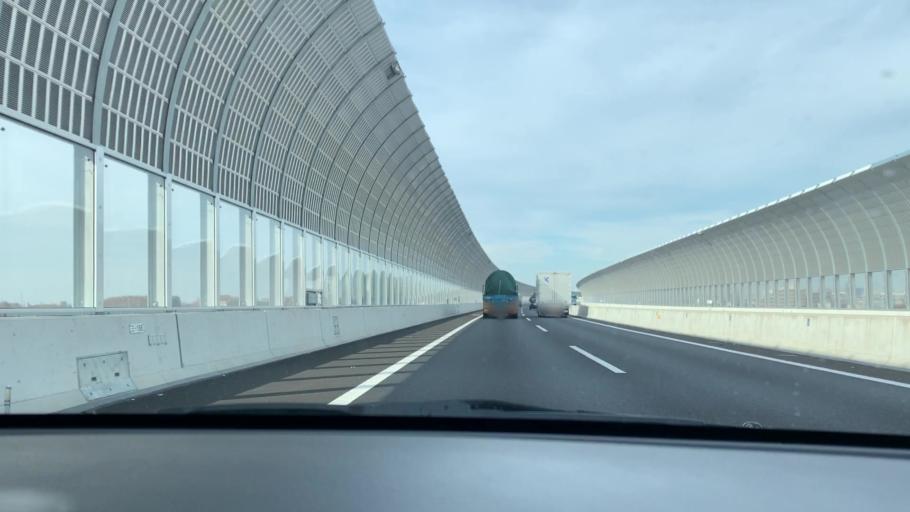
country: JP
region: Chiba
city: Matsudo
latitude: 35.7839
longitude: 139.8826
